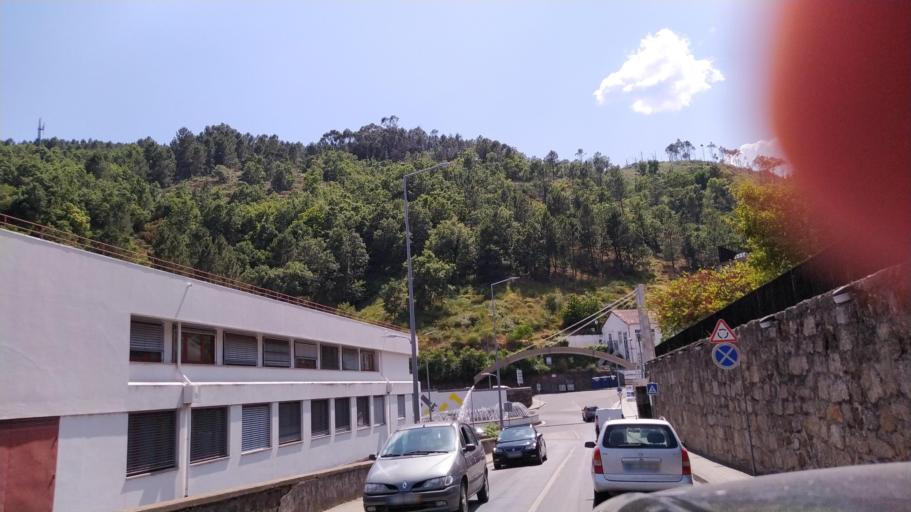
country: PT
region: Castelo Branco
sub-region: Covilha
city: Covilha
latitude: 40.2777
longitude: -7.5098
